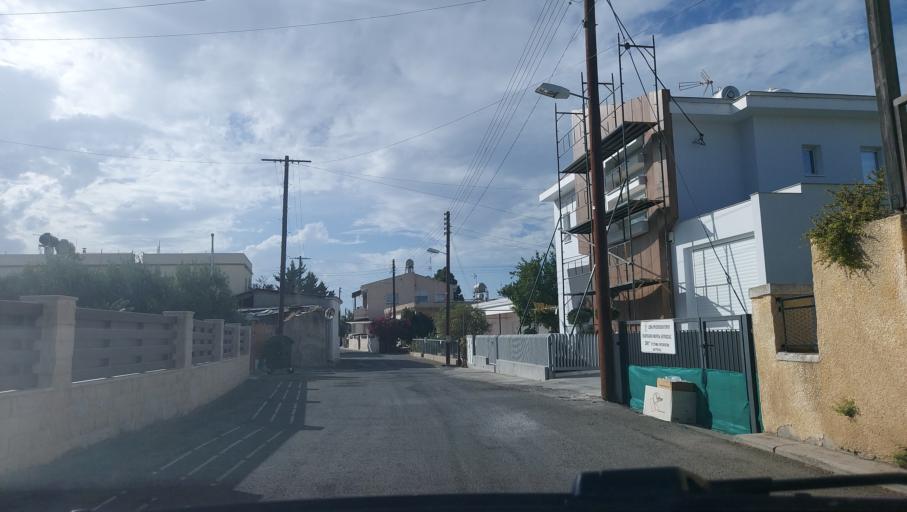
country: CY
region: Lefkosia
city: Pano Deftera
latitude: 35.0843
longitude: 33.2663
